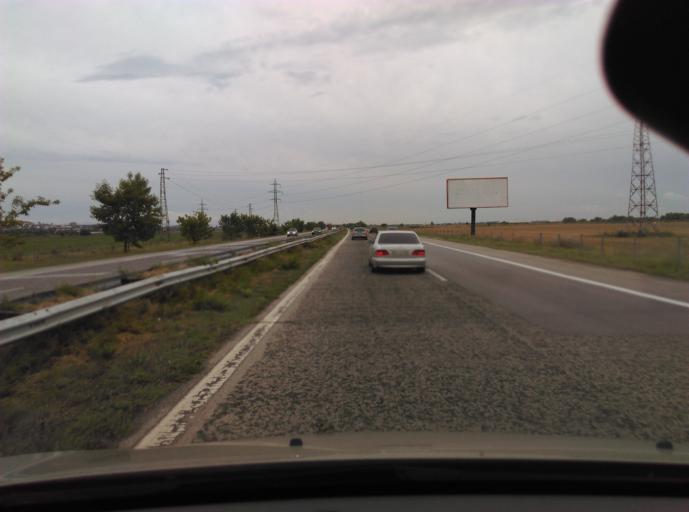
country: BG
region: Plovdiv
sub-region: Obshtina Rakovski
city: Rakovski
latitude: 42.2136
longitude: 24.9830
